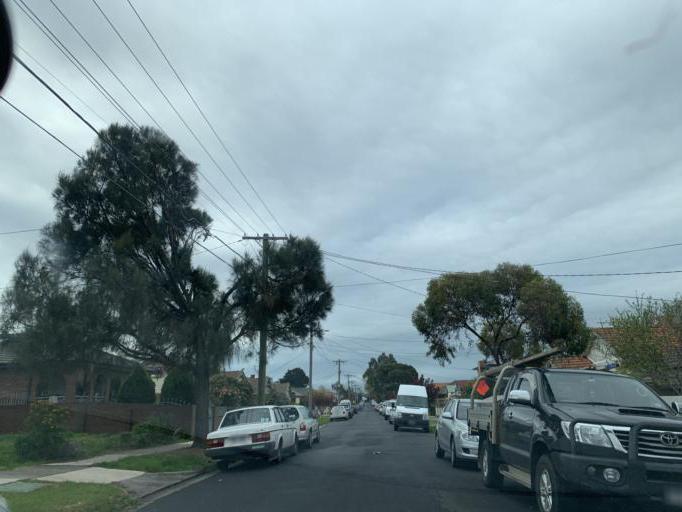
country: AU
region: Victoria
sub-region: Moreland
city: Coburg
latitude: -37.7500
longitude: 144.9738
